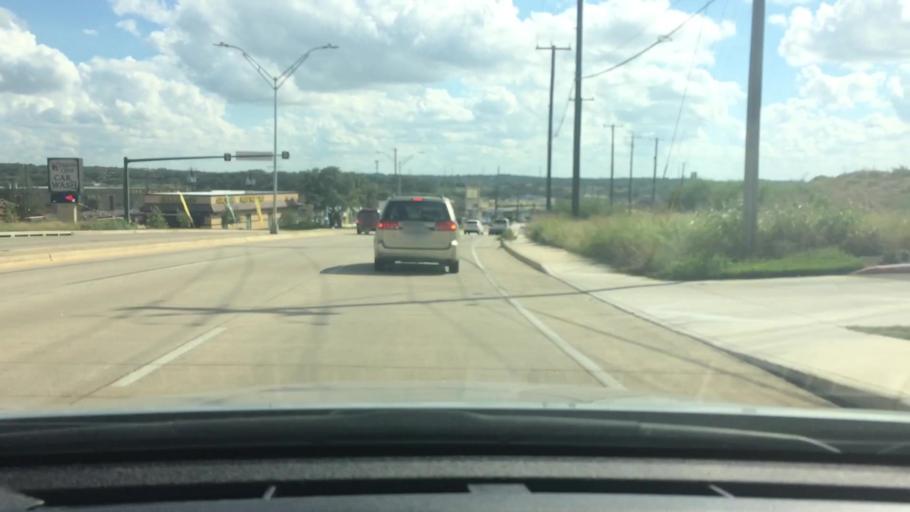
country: US
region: Texas
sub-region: Bexar County
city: Hollywood Park
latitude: 29.6070
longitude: -98.4186
